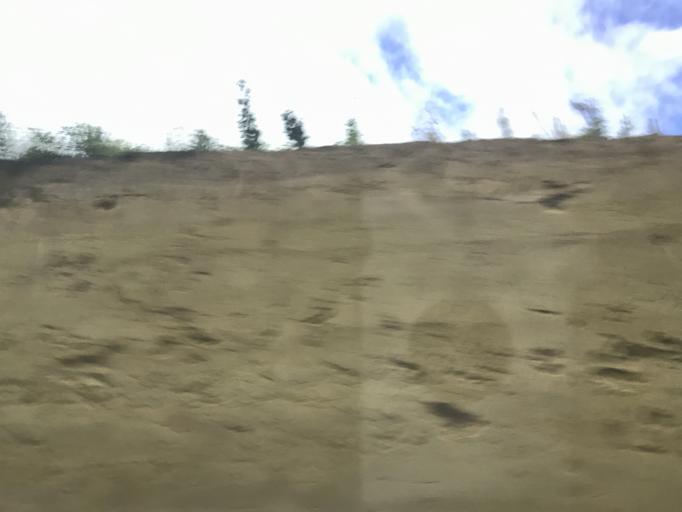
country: GT
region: Chimaltenango
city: Parramos
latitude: 14.6262
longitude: -90.8070
